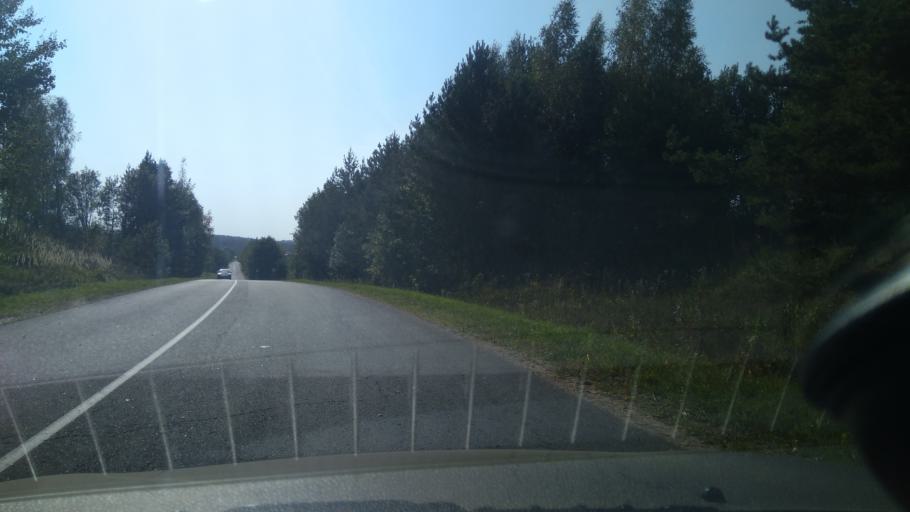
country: BY
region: Minsk
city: Rakaw
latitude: 54.0177
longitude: 27.0500
